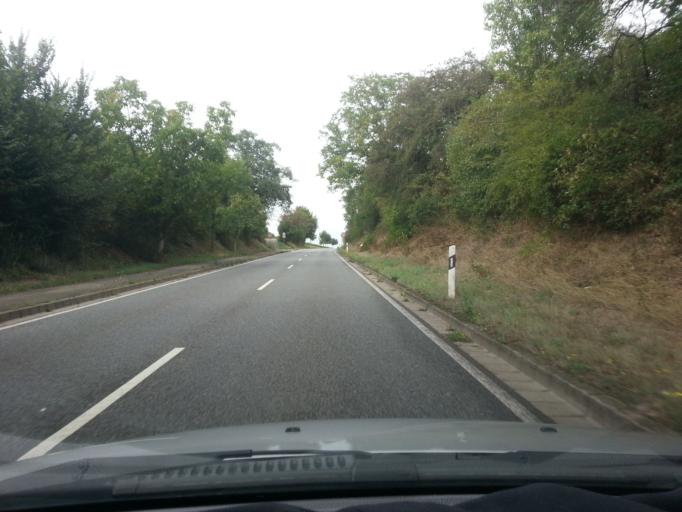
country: DE
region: Rheinland-Pfalz
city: Essingen
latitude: 49.2268
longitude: 8.1785
